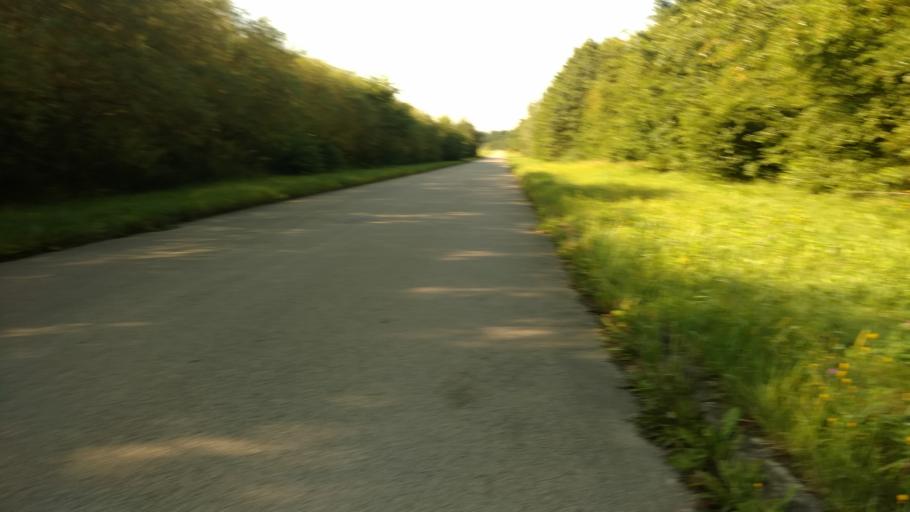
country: PL
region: Silesian Voivodeship
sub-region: Powiat pszczynski
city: Pszczyna
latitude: 49.9874
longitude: 18.9710
